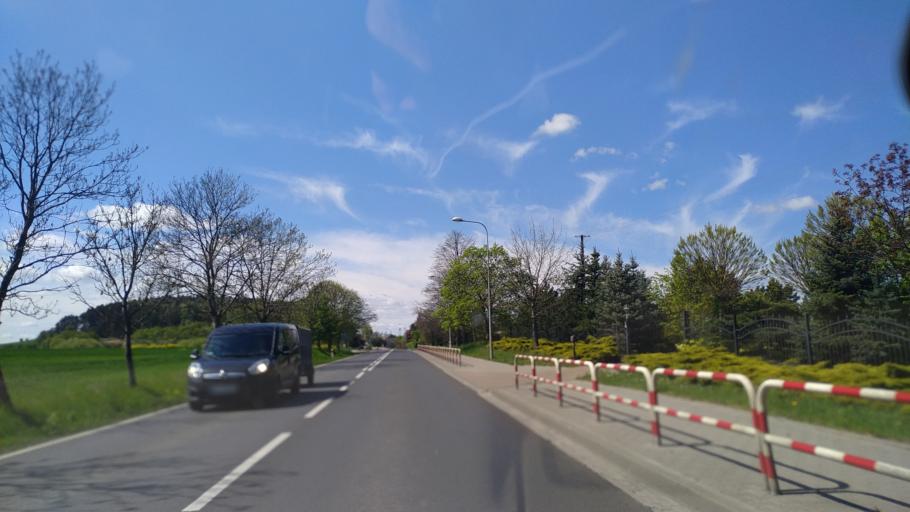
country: PL
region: Greater Poland Voivodeship
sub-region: Powiat pilski
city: Szydlowo
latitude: 53.2391
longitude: 16.6437
